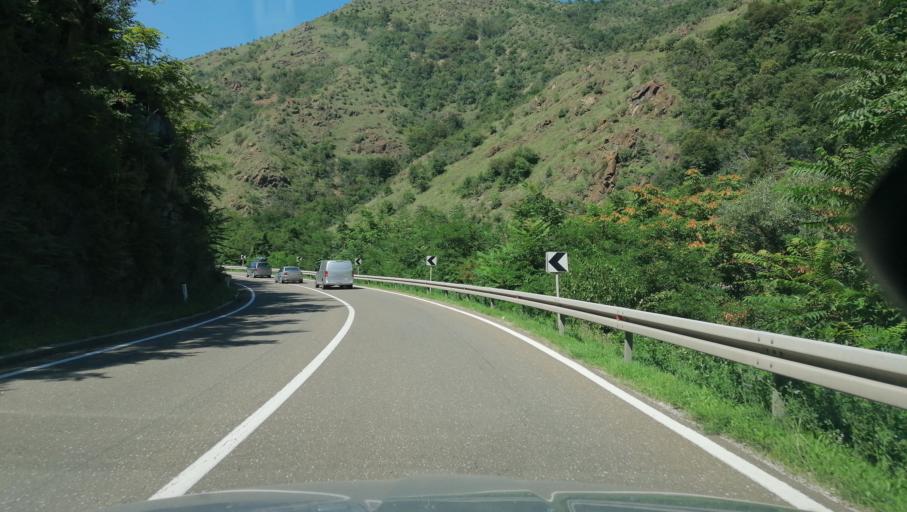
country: RS
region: Central Serbia
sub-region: Raski Okrug
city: Kraljevo
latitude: 43.5864
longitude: 20.5808
